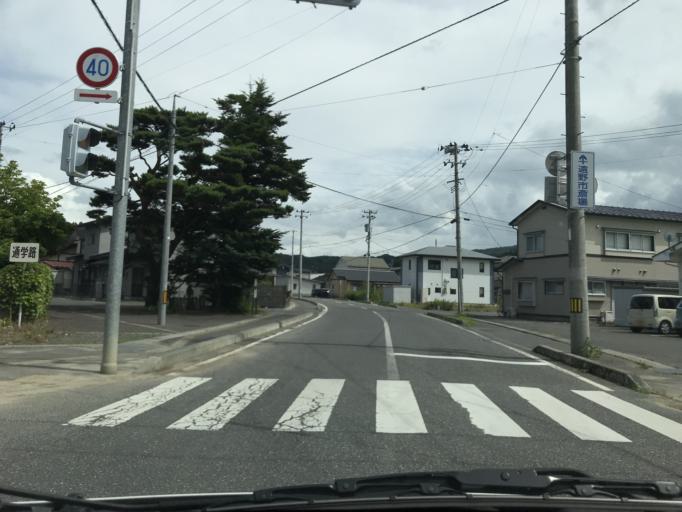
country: JP
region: Iwate
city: Tono
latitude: 39.3264
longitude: 141.5338
